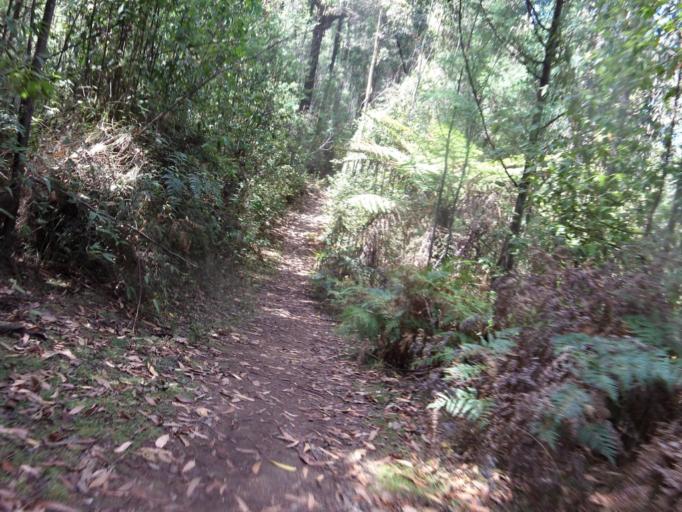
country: AU
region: Victoria
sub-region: Yarra Ranges
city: Healesville
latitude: -37.4140
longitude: 145.5649
